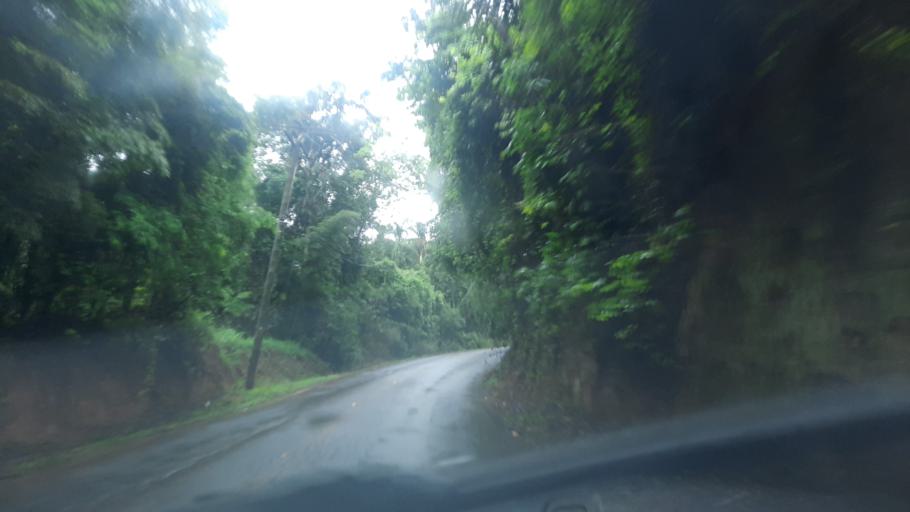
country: BR
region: Sao Paulo
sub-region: Atibaia
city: Atibaia
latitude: -23.0814
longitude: -46.5251
